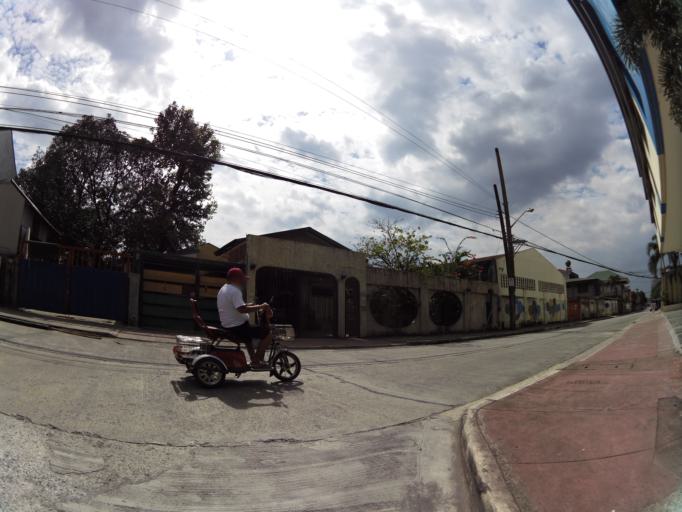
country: PH
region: Metro Manila
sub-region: Marikina
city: Calumpang
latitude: 14.6257
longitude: 121.1018
